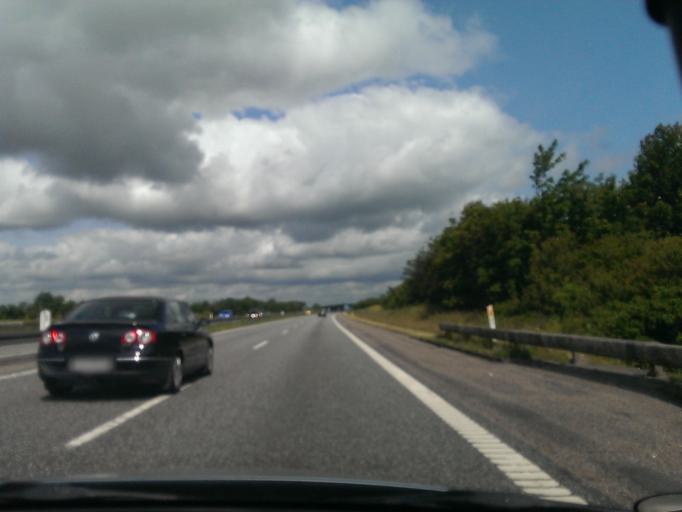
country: DK
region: North Denmark
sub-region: Mariagerfjord Kommune
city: Hobro
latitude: 56.5582
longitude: 9.8683
